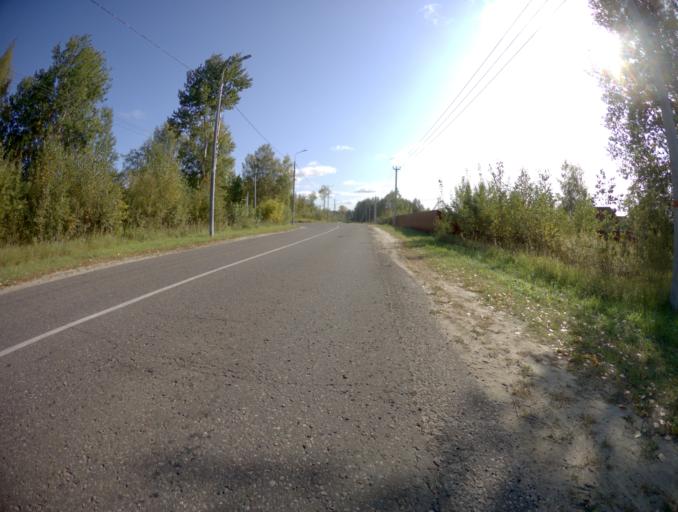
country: RU
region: Moskovskaya
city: Roshal'
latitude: 55.6718
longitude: 39.8553
